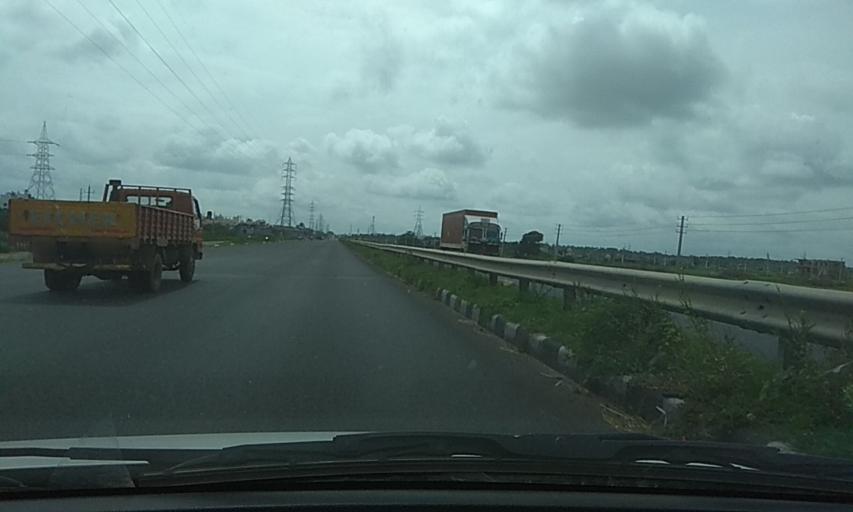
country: IN
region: Karnataka
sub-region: Davanagere
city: Harihar
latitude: 14.4373
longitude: 75.9084
